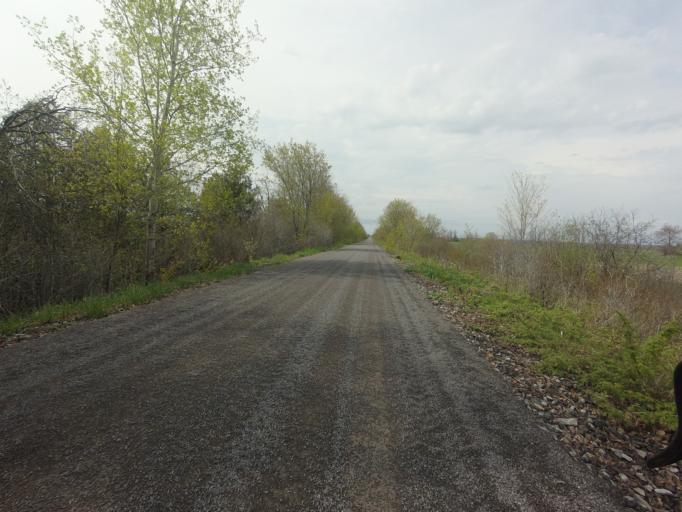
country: CA
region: Ontario
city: Carleton Place
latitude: 45.1661
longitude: -76.1487
